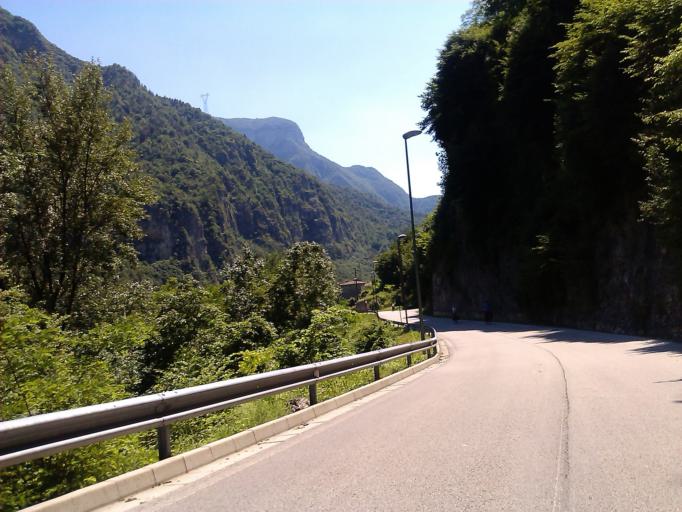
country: IT
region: Veneto
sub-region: Provincia di Vicenza
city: Cismon del Grappa
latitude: 45.8955
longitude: 11.6896
